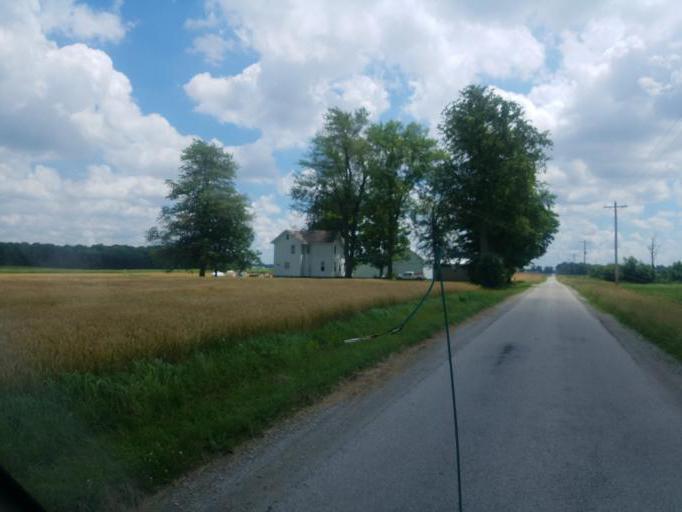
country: US
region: Ohio
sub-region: Huron County
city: Willard
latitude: 41.0237
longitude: -82.8305
